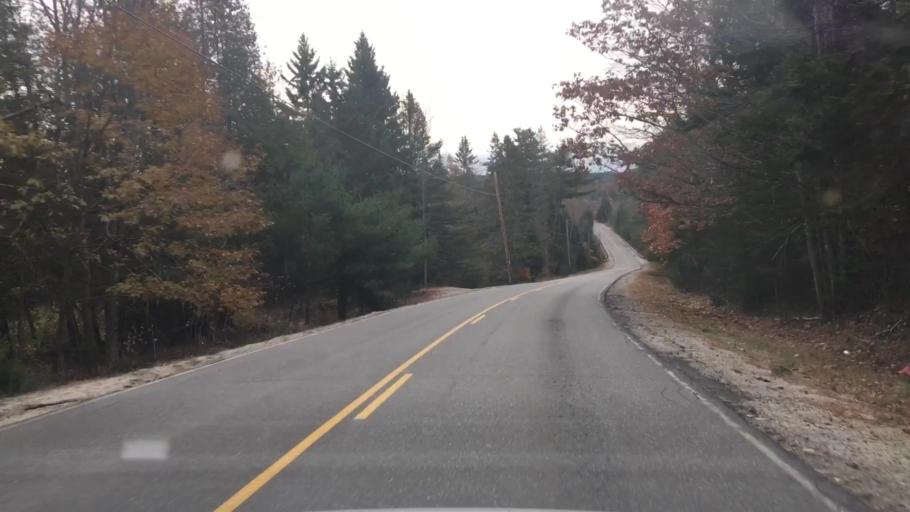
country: US
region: Maine
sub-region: Hancock County
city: Penobscot
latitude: 44.4287
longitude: -68.6254
